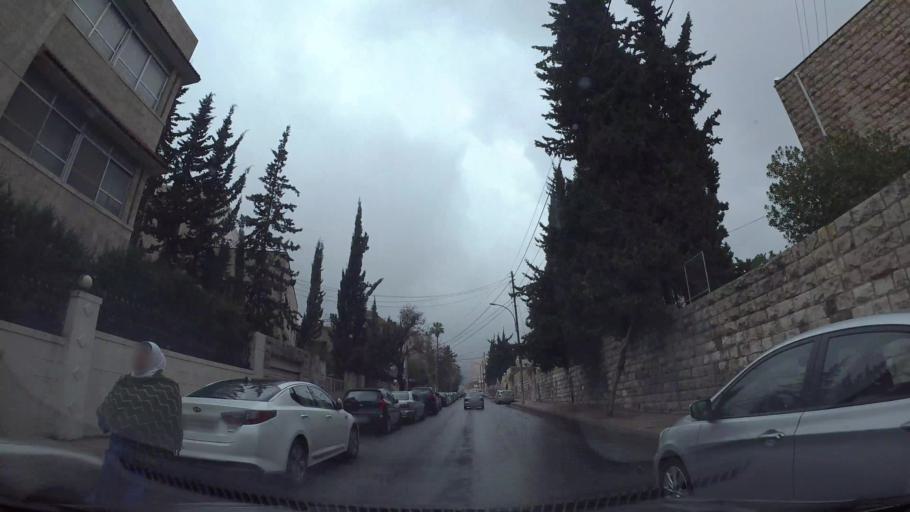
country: JO
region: Amman
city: Amman
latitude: 31.9492
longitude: 35.9193
